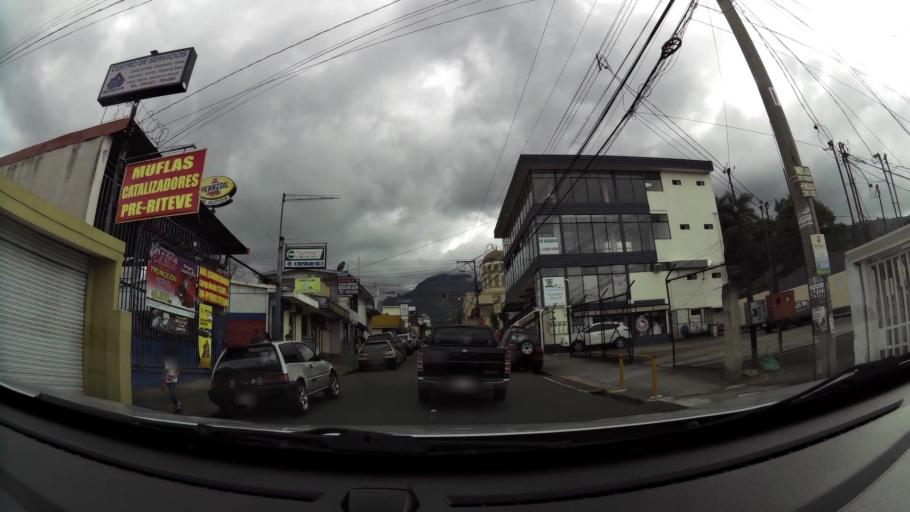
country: CR
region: San Jose
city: Escazu
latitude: 9.9208
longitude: -84.1391
